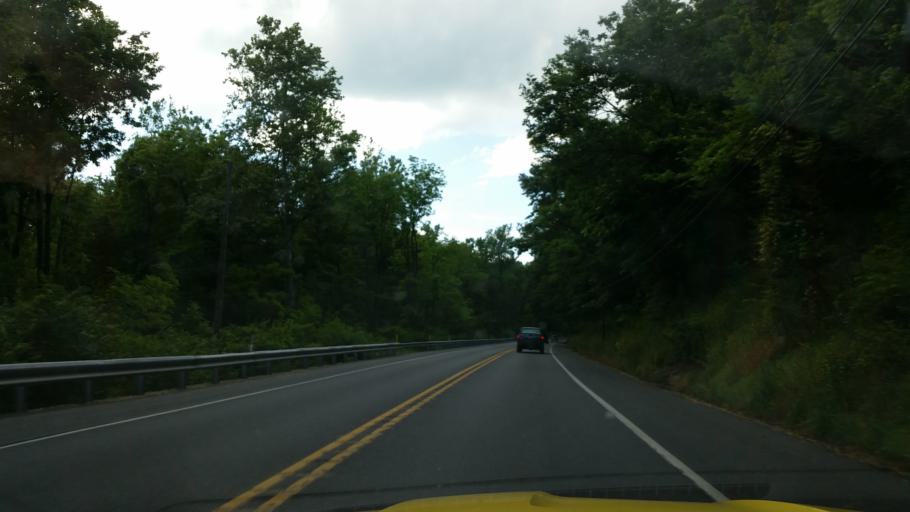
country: US
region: Pennsylvania
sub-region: Lancaster County
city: Brickerville
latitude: 40.2125
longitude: -76.3013
